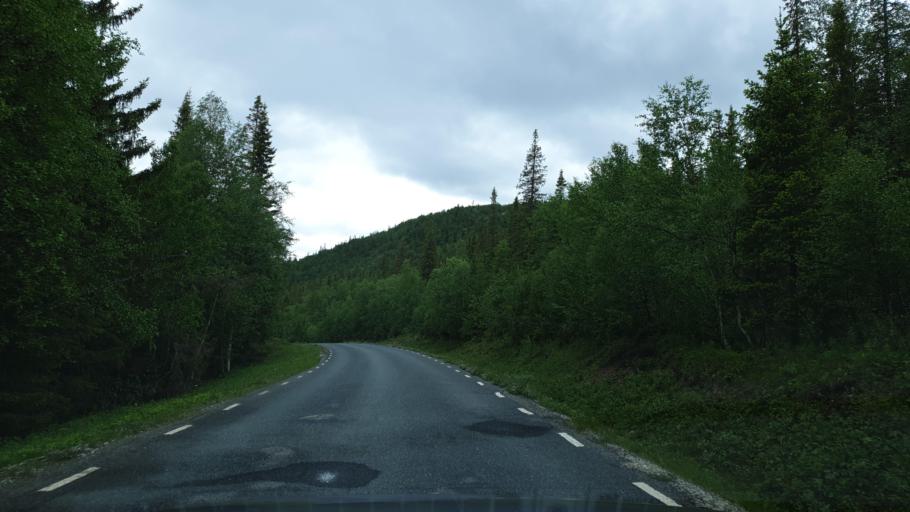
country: SE
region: Vaesterbotten
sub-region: Vilhelmina Kommun
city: Sjoberg
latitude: 65.2572
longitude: 15.4030
